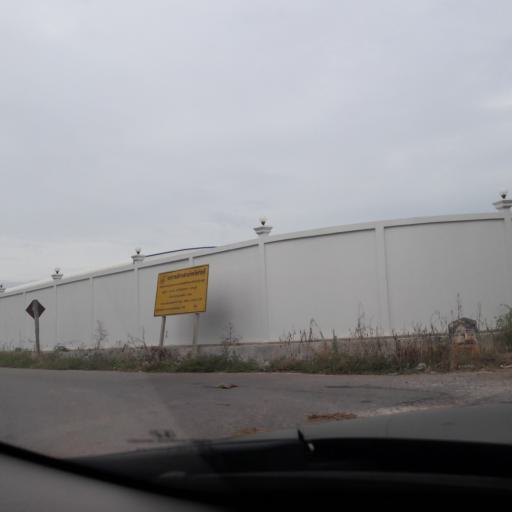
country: TH
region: Ratchaburi
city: Damnoen Saduak
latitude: 13.5605
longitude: 99.9502
